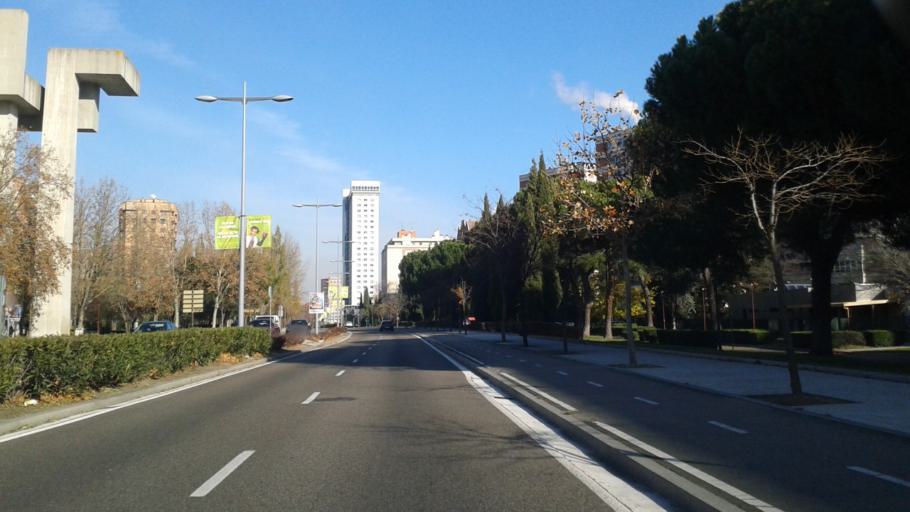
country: ES
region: Castille and Leon
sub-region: Provincia de Valladolid
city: Valladolid
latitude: 41.6548
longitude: -4.7368
